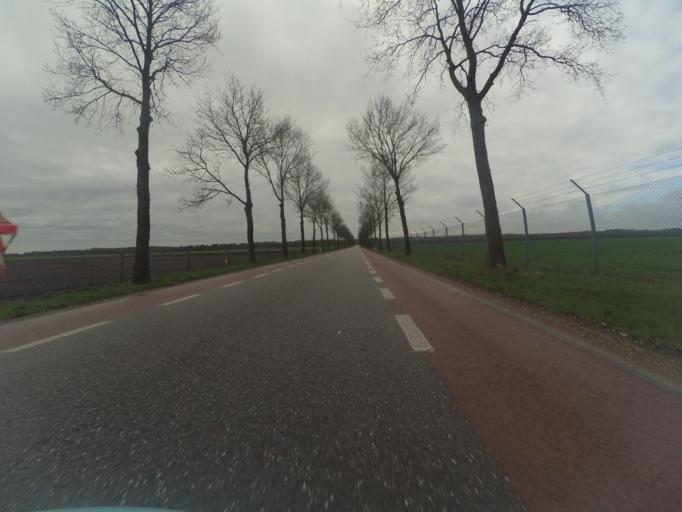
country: NL
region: Gelderland
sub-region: Gemeente Arnhem
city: Gulden Bodem
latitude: 52.0559
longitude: 5.8988
